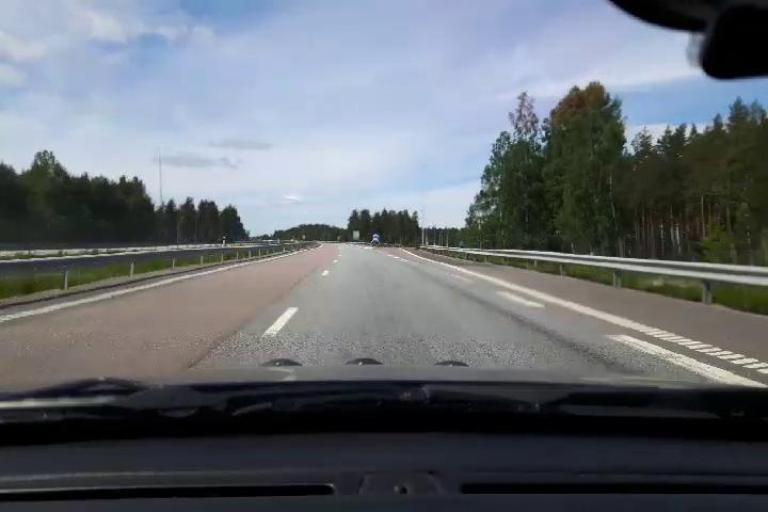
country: SE
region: Gaevleborg
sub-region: Gavle Kommun
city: Gavle
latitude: 60.6365
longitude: 17.1439
